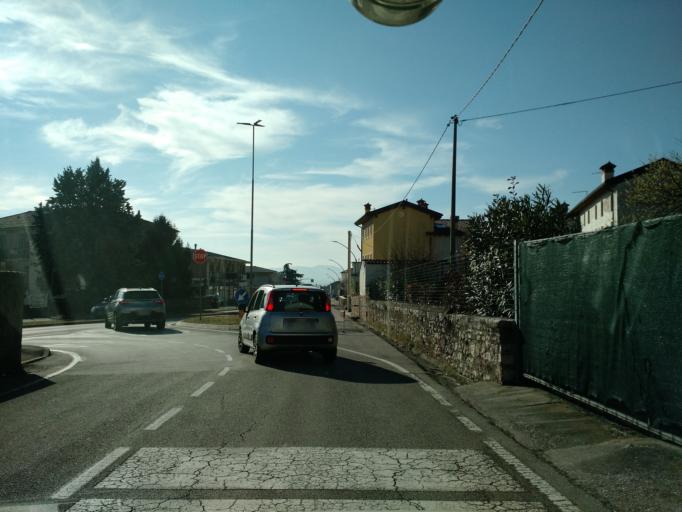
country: IT
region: Veneto
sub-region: Provincia di Vicenza
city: Piovene Rocchette
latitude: 45.7547
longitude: 11.4299
